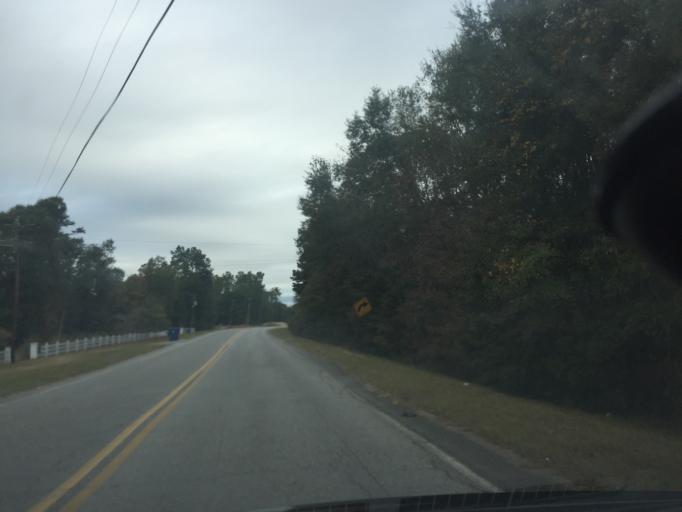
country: US
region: Georgia
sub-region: Chatham County
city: Bloomingdale
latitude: 32.1116
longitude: -81.3854
